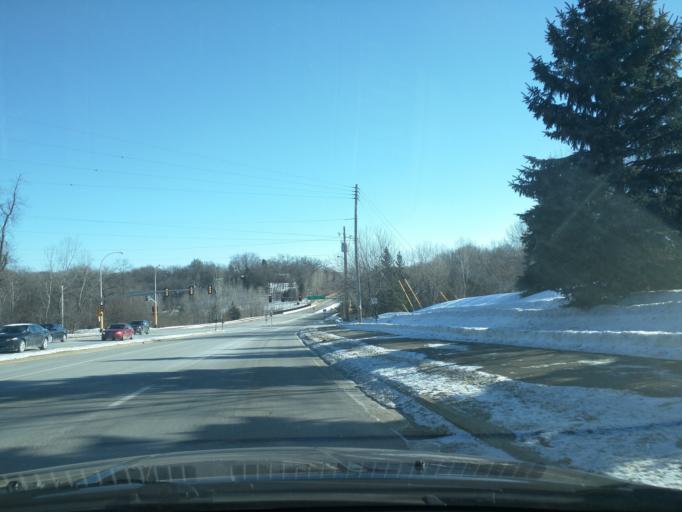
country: US
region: Minnesota
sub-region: Hennepin County
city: Minnetonka
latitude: 44.8922
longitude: -93.4937
